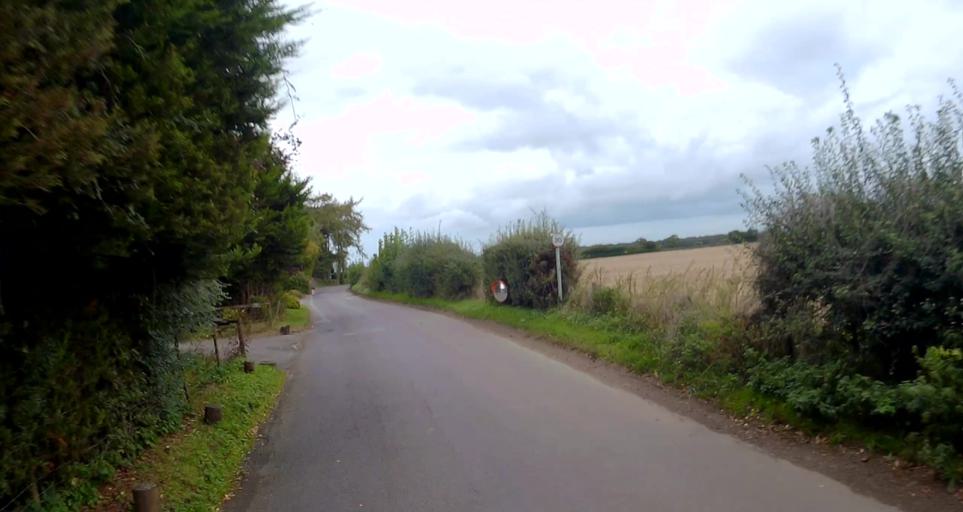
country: GB
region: England
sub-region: Hampshire
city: Four Marks
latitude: 51.1325
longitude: -1.0740
